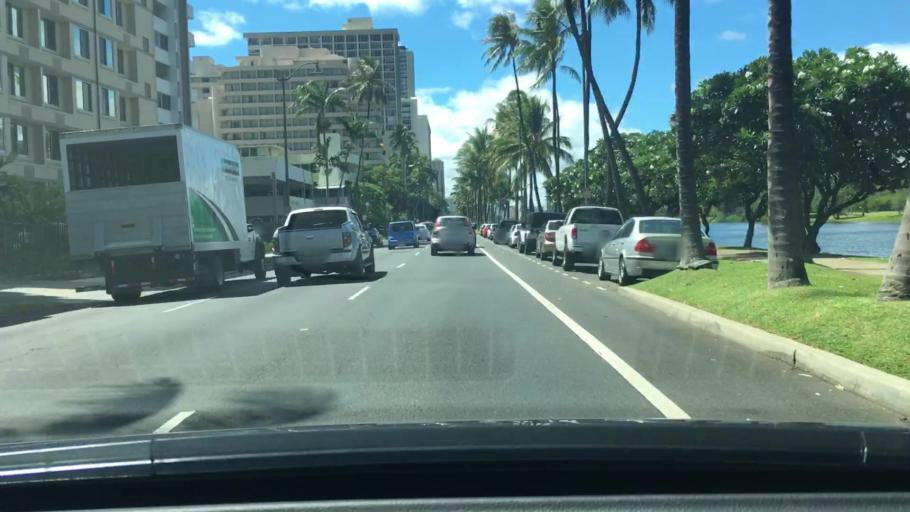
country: US
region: Hawaii
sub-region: Honolulu County
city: Honolulu
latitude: 21.2779
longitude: -157.8215
